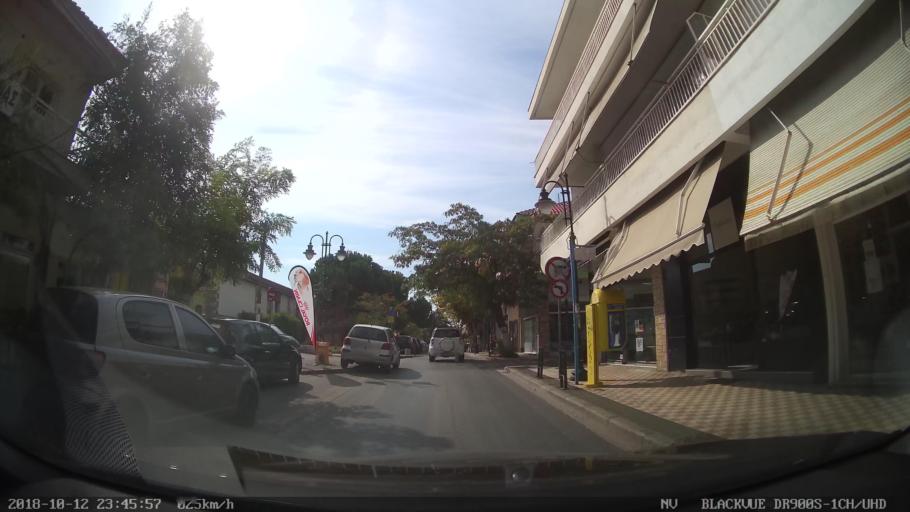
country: GR
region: Central Macedonia
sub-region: Nomos Thessalonikis
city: Pylaia
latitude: 40.6004
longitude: 22.9887
